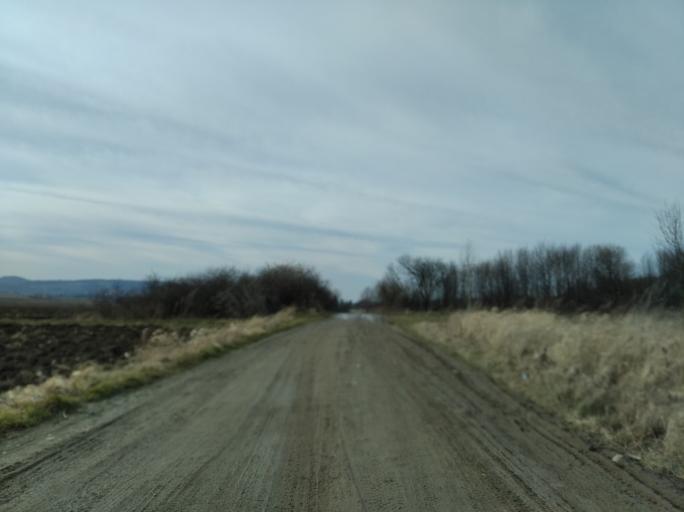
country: PL
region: Subcarpathian Voivodeship
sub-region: Powiat brzozowski
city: Turze Pole
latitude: 49.6575
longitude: 22.0215
